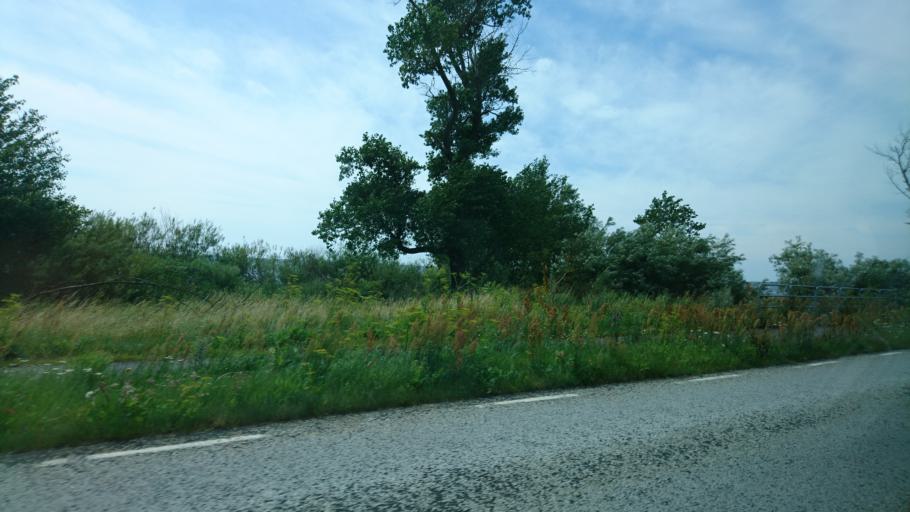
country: SE
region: Skane
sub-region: Skurups Kommun
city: Skivarp
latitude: 55.3881
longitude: 13.5387
